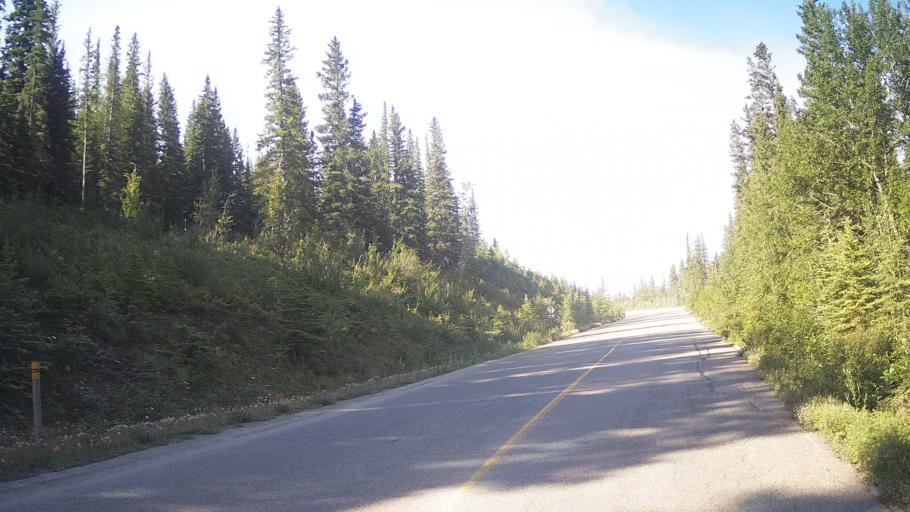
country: CA
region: Alberta
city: Jasper Park Lodge
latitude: 53.2045
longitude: -117.9220
